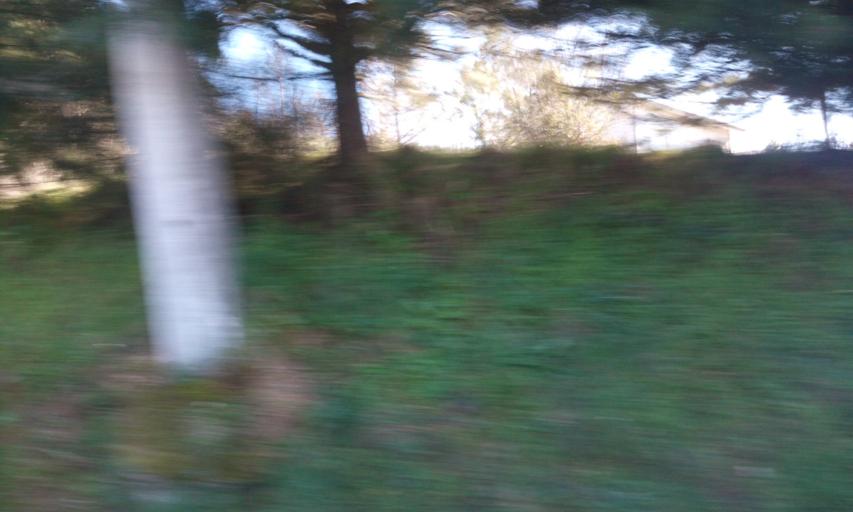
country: PT
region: Guarda
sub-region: Manteigas
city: Manteigas
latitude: 40.4780
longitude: -7.6175
